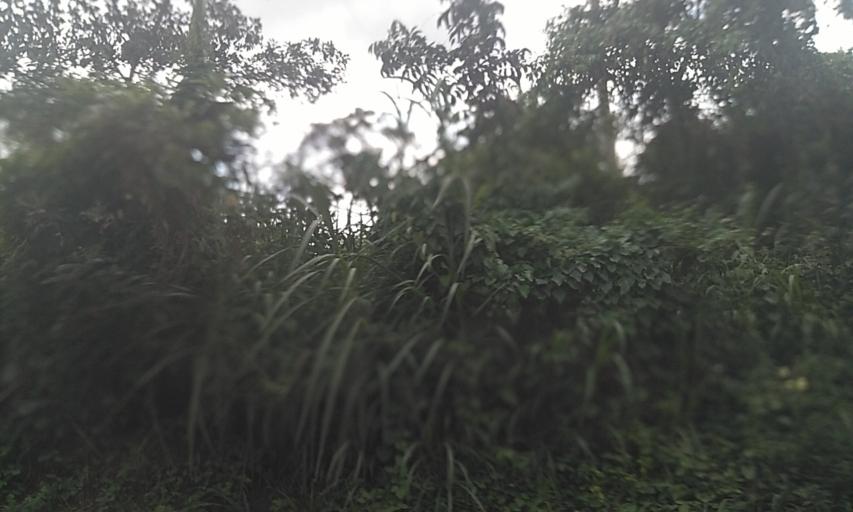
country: UG
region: Central Region
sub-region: Wakiso District
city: Wakiso
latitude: 0.3556
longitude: 32.4601
